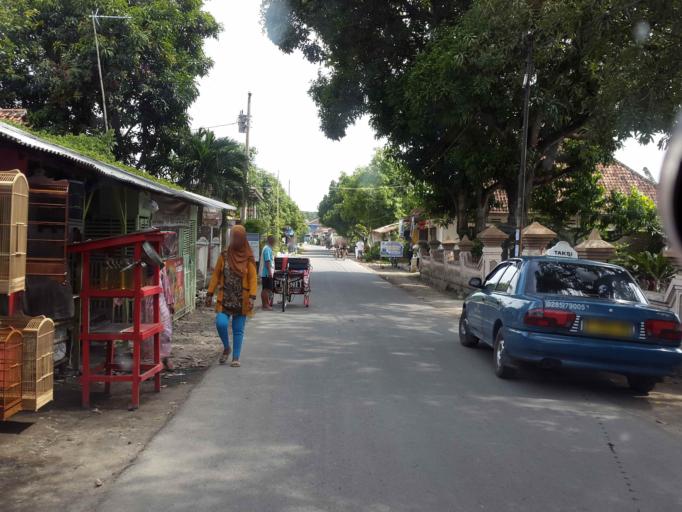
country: ID
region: Central Java
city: Petarukan
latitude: -6.8949
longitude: 109.4539
